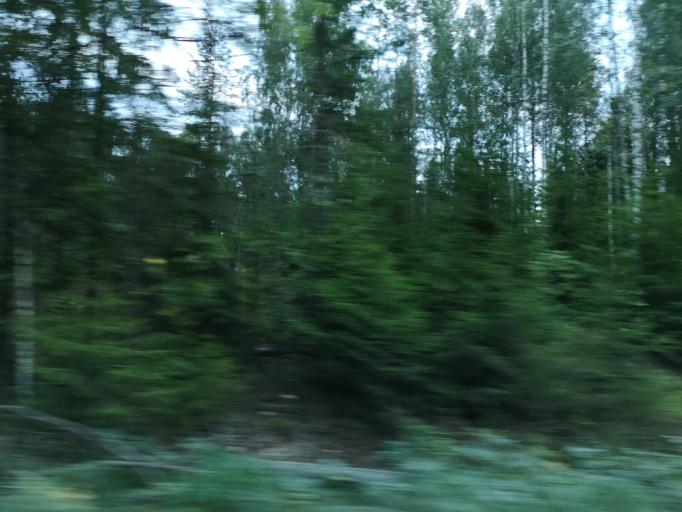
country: FI
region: Central Finland
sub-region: Jyvaeskylae
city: Toivakka
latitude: 62.0910
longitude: 26.0738
